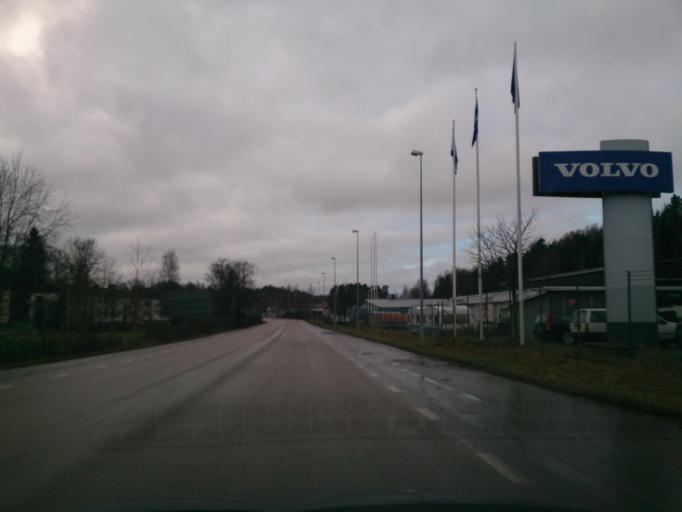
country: SE
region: OEstergoetland
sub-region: Atvidabergs Kommun
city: Atvidaberg
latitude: 58.2033
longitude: 15.9995
